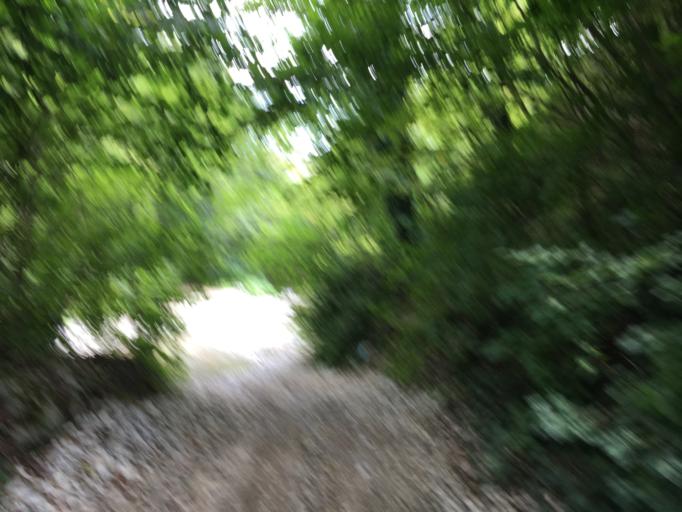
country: RU
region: Krasnodarskiy
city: Tuapse
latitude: 44.2596
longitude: 39.2175
